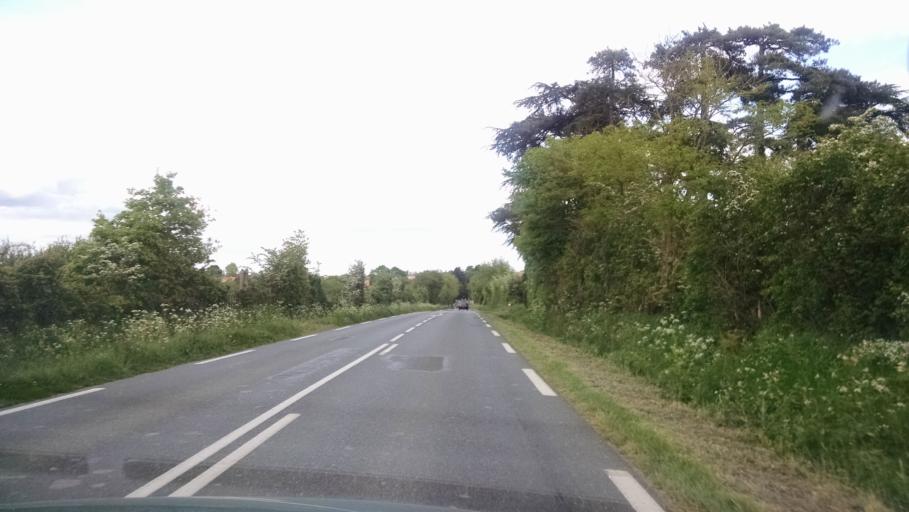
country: FR
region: Pays de la Loire
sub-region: Departement de la Loire-Atlantique
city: Gorges
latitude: 47.0917
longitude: -1.3162
